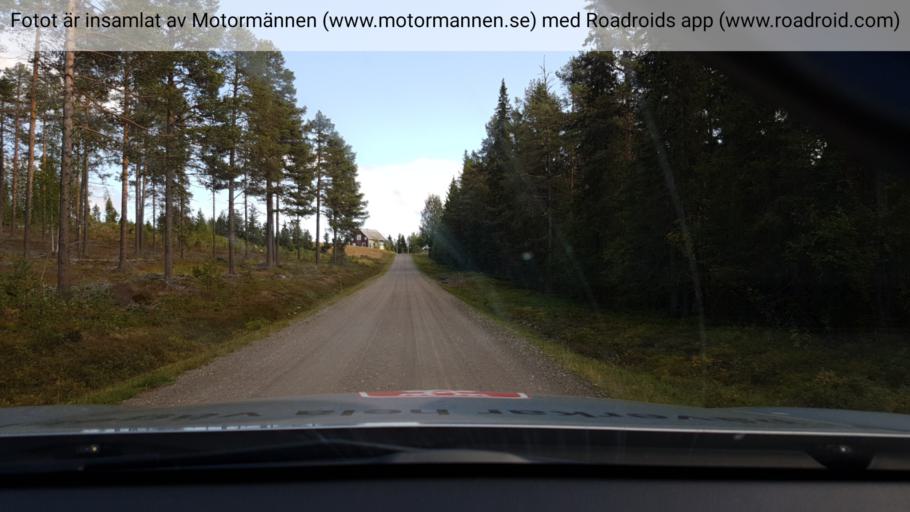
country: SE
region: Vaesterbotten
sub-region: Mala Kommun
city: Mala
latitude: 65.3394
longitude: 18.8225
